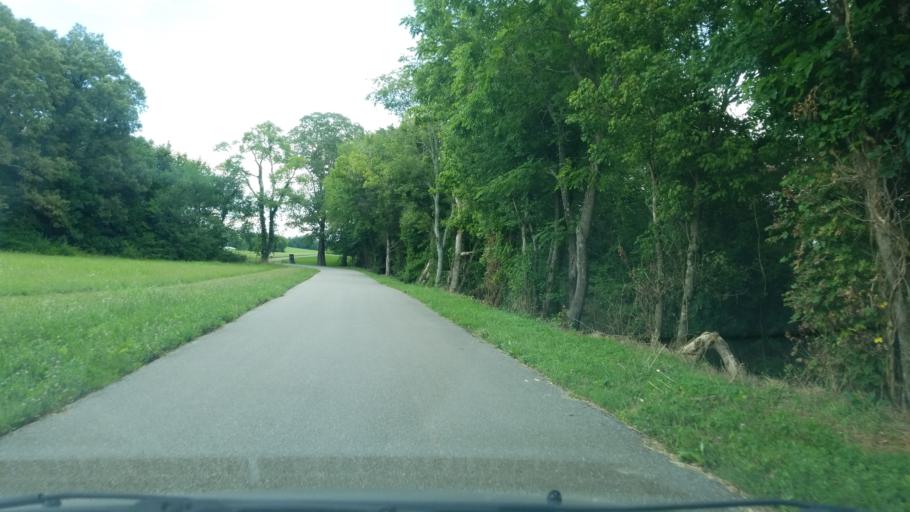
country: US
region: Tennessee
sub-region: Monroe County
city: Sweetwater
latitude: 35.6395
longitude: -84.5074
